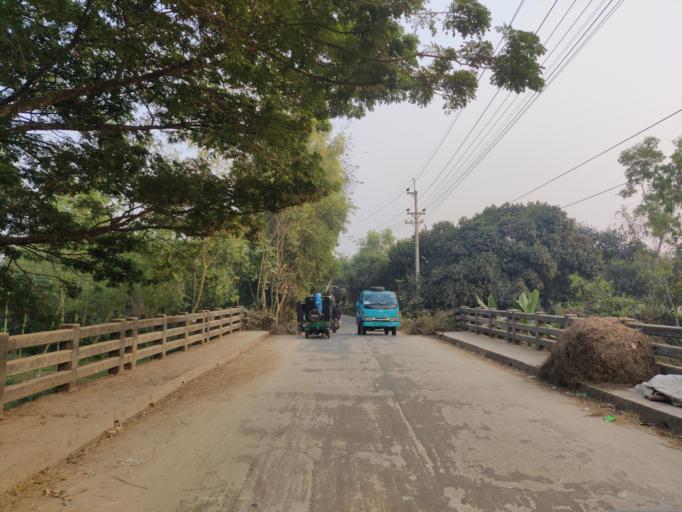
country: BD
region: Dhaka
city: Bajitpur
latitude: 24.1567
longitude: 90.7690
